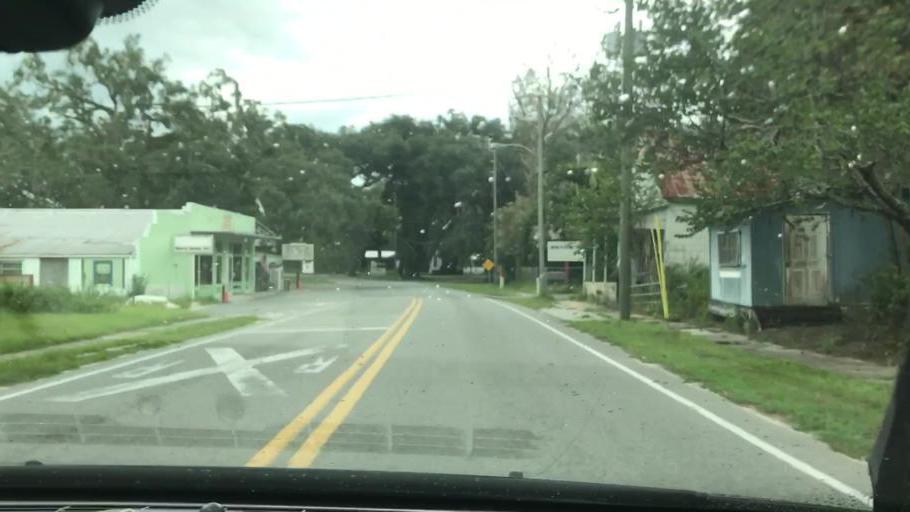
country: US
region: Florida
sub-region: Madison County
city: Madison
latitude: 30.4185
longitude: -83.3006
